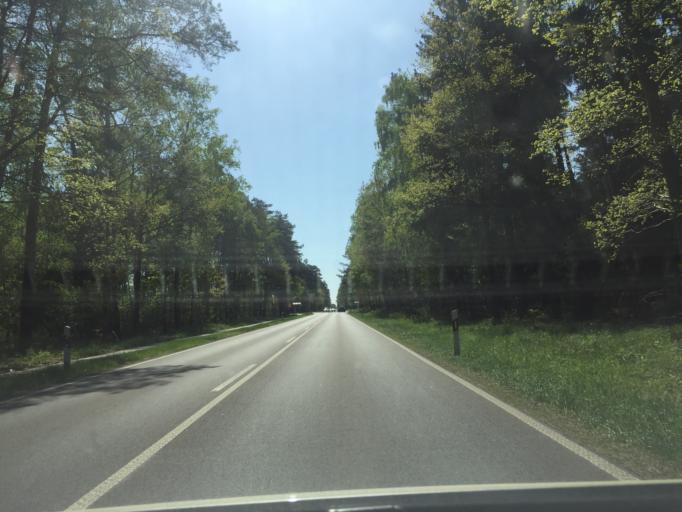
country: DE
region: Mecklenburg-Vorpommern
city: Torgelow
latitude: 53.6182
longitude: 14.0303
